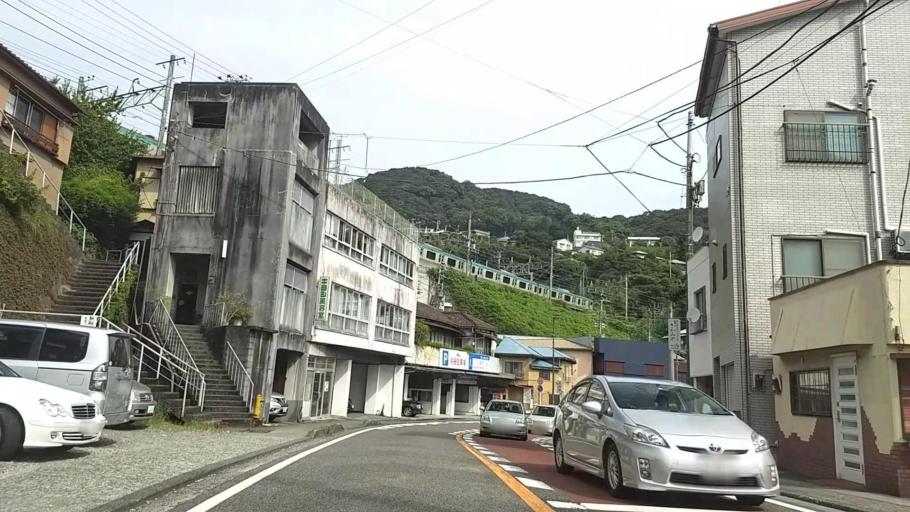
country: JP
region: Shizuoka
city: Atami
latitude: 35.1106
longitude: 139.0844
